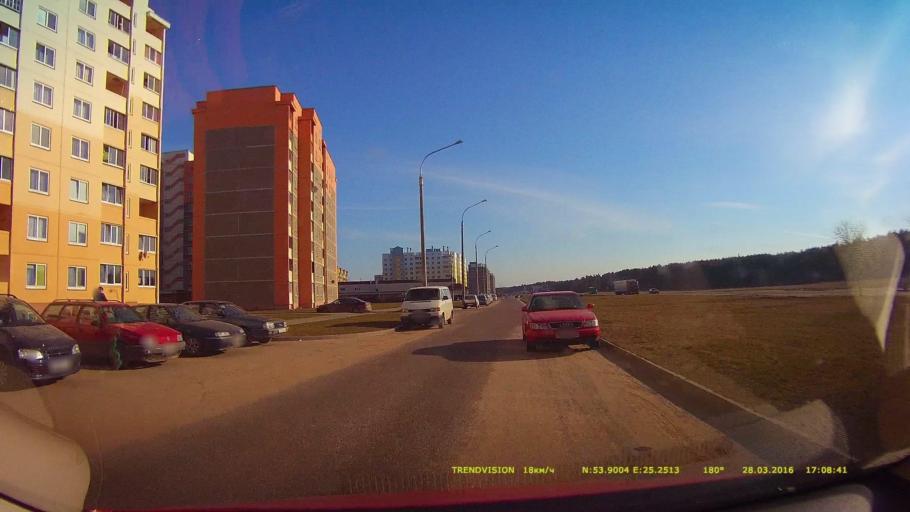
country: BY
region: Grodnenskaya
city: Lida
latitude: 53.9002
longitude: 25.2513
